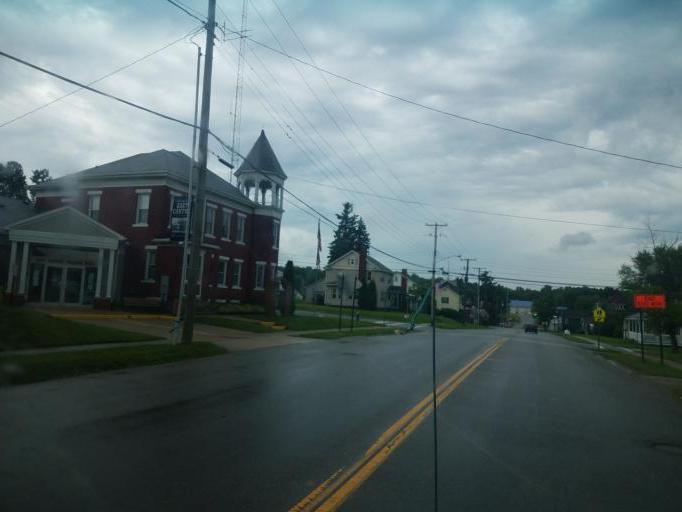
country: US
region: Ohio
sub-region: Stark County
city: East Canton
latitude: 40.7867
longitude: -81.2841
